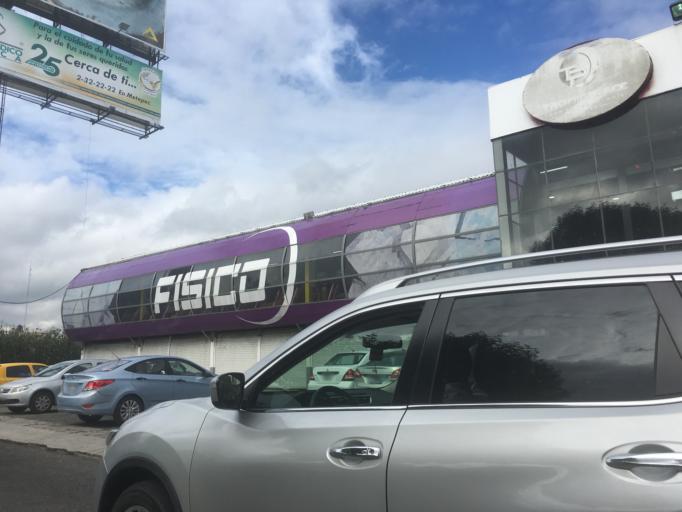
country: MX
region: Morelos
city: Metepec
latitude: 19.2656
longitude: -99.6075
